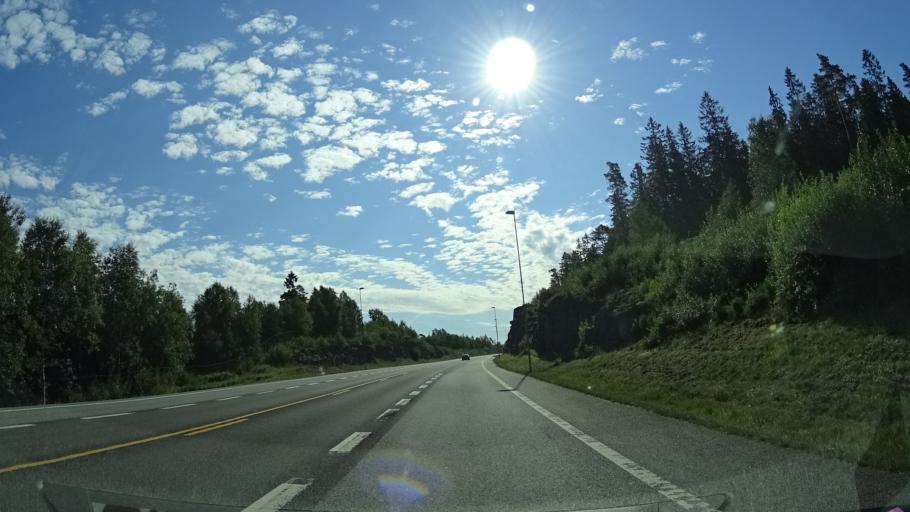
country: NO
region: Ostfold
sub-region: Eidsberg
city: Mysen
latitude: 59.5456
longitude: 11.4695
